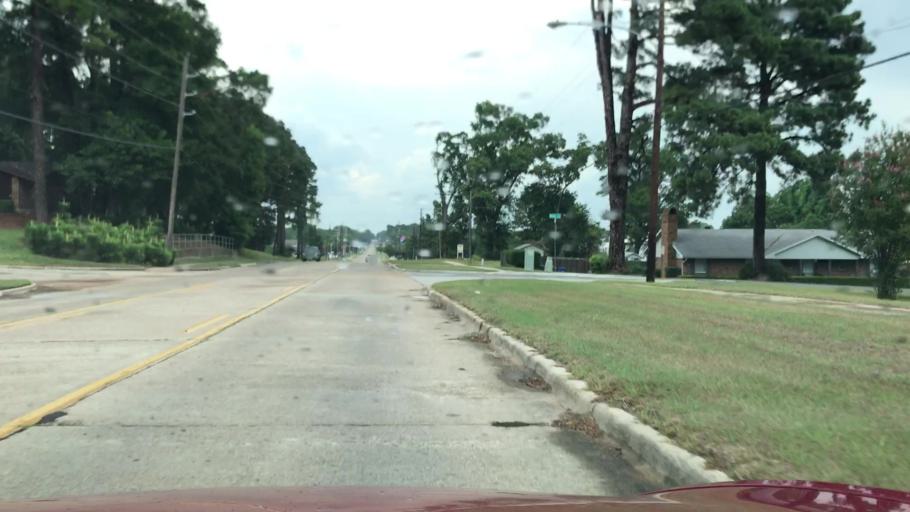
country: US
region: Louisiana
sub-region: De Soto Parish
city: Stonewall
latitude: 32.3980
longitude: -93.7804
